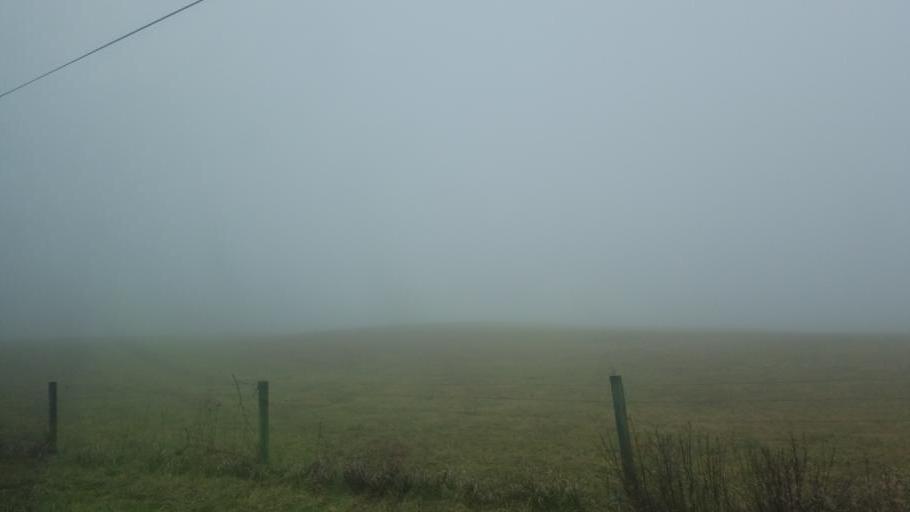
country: US
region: Ohio
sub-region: Champaign County
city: North Lewisburg
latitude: 40.2941
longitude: -83.6380
